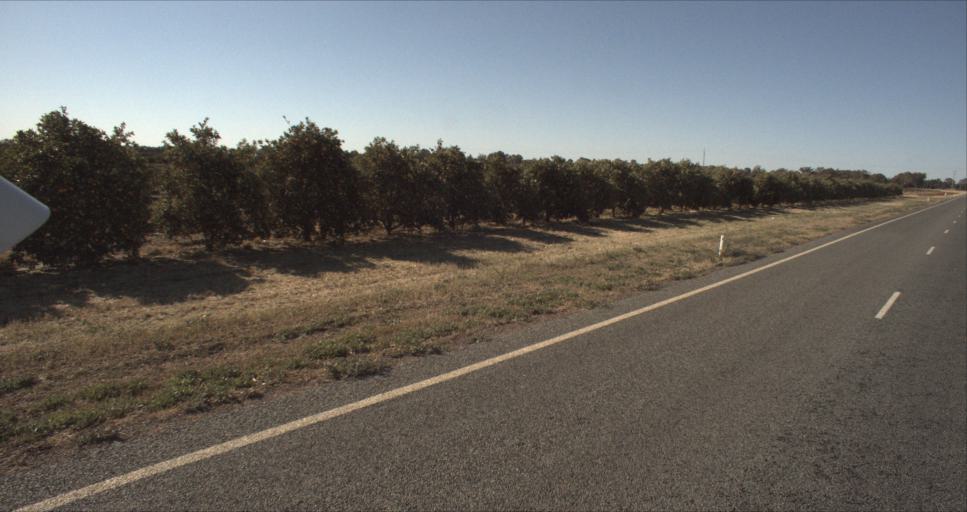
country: AU
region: New South Wales
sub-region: Leeton
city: Leeton
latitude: -34.6168
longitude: 146.4002
